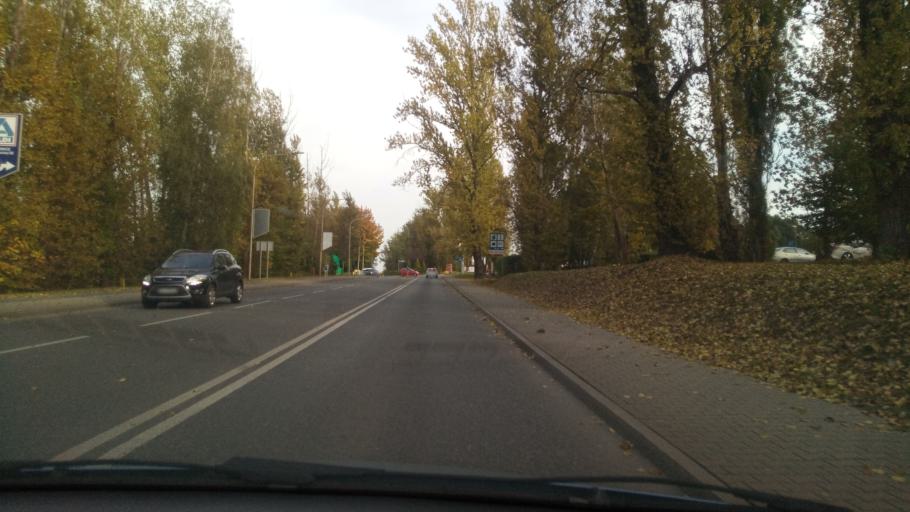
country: PL
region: Silesian Voivodeship
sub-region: Sosnowiec
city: Sosnowiec
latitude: 50.2480
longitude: 19.1215
